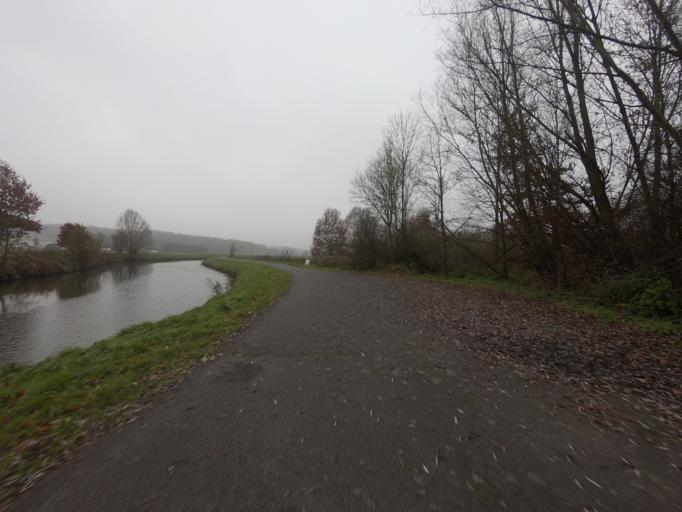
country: BE
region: Flanders
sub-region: Provincie Oost-Vlaanderen
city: Geraardsbergen
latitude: 50.7546
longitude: 3.8598
